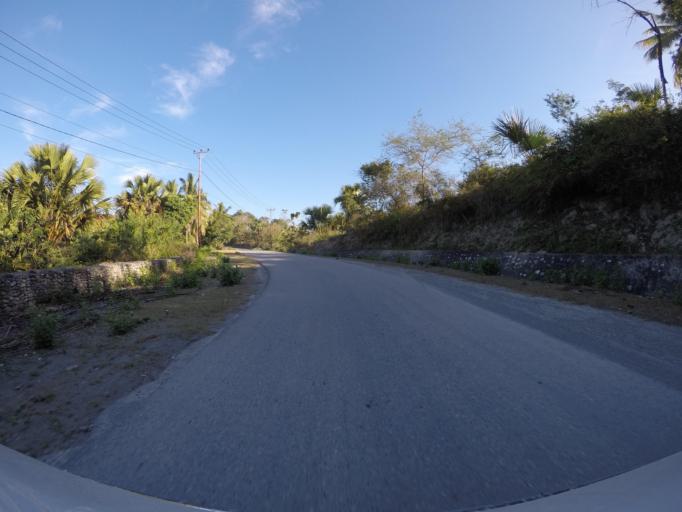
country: TL
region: Viqueque
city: Viqueque
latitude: -8.8713
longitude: 126.3518
